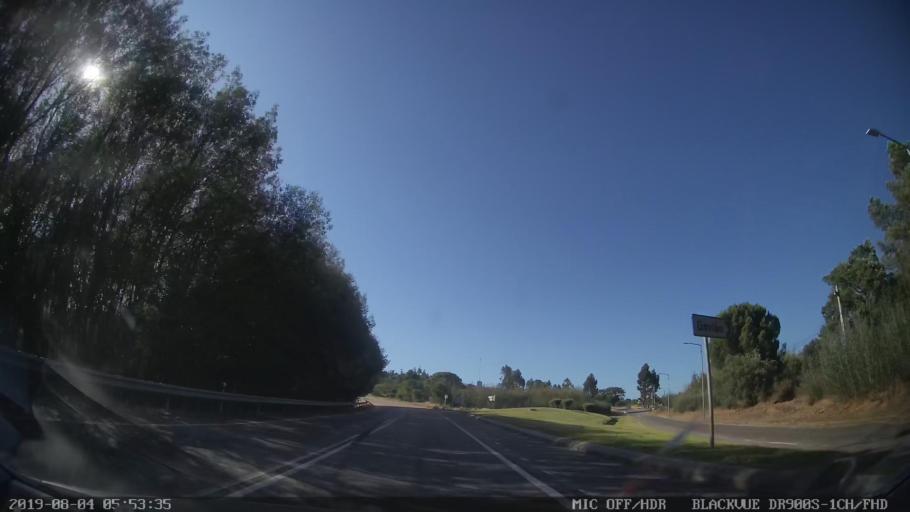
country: PT
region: Portalegre
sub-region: Gaviao
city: Gaviao
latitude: 39.4559
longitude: -7.9314
